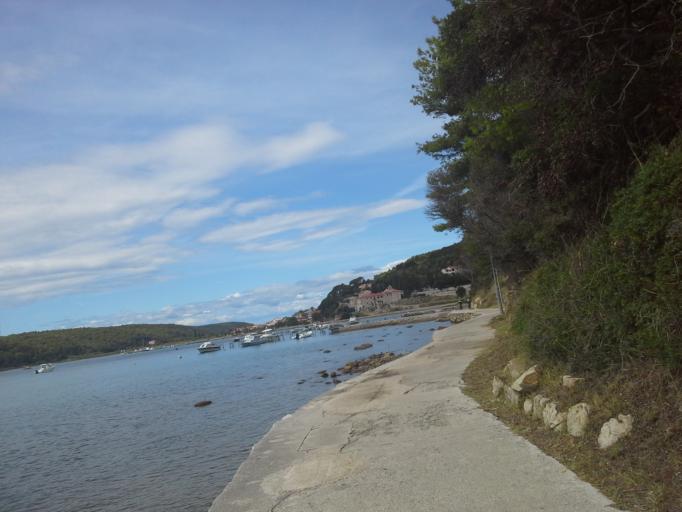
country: HR
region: Primorsko-Goranska
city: Kampor
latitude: 44.7657
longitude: 14.7442
